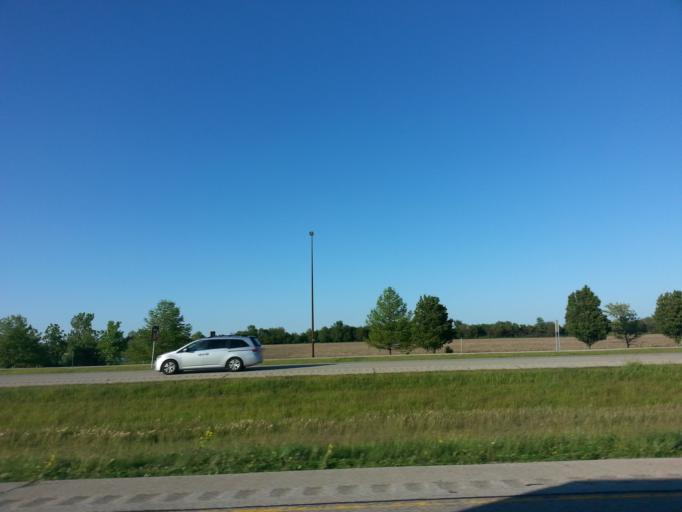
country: US
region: Illinois
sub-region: De Witt County
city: Farmer City
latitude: 40.2682
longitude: -88.6682
